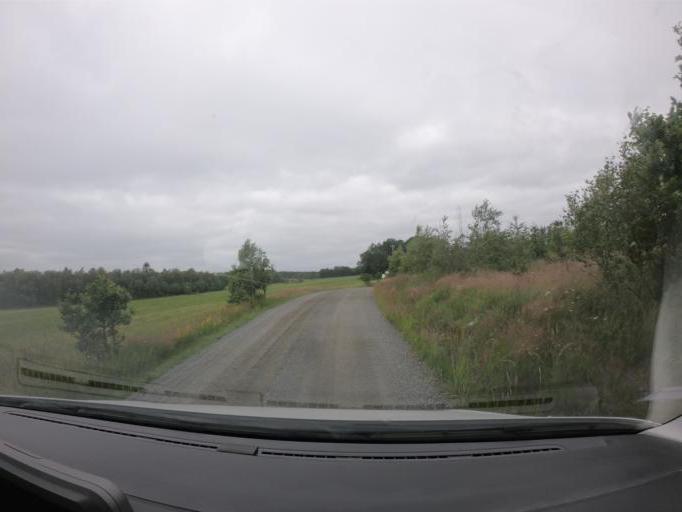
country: SE
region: Skane
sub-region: Hoors Kommun
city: Hoeoer
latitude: 56.0094
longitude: 13.4748
